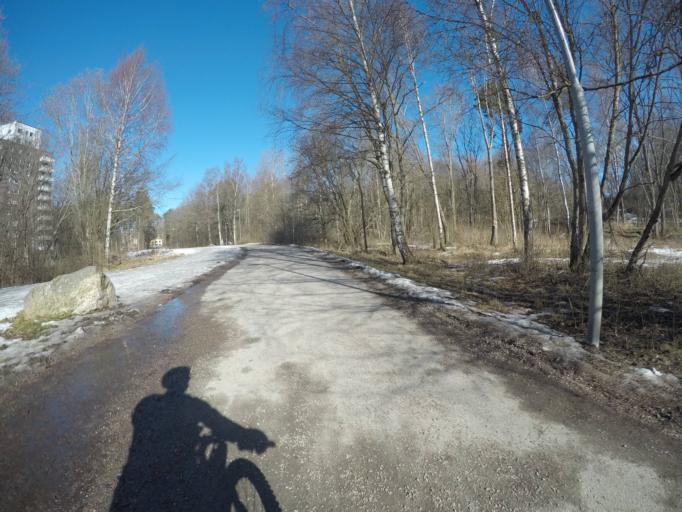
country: SE
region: Vaestmanland
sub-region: Vasteras
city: Vasteras
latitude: 59.6028
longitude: 16.5802
